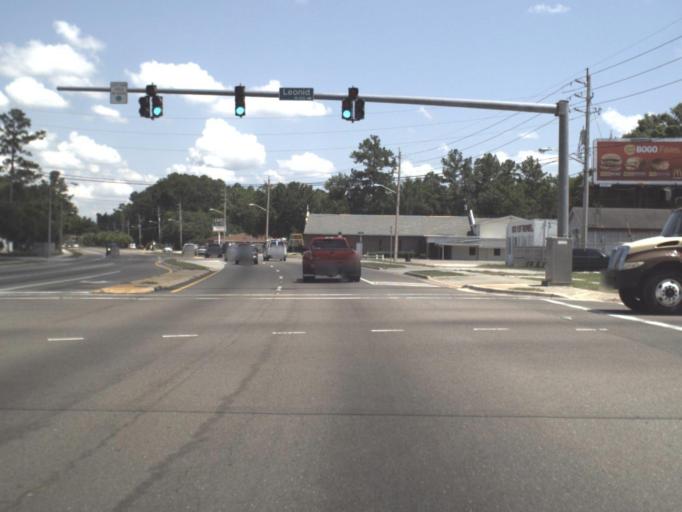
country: US
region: Florida
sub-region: Duval County
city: Jacksonville
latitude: 30.4296
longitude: -81.6940
